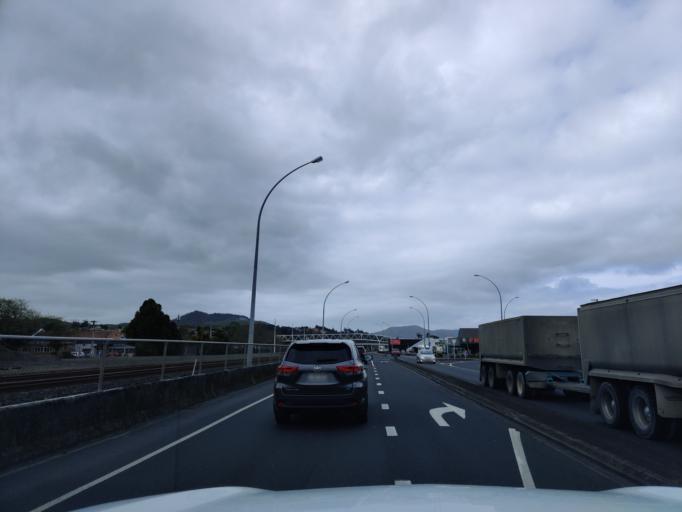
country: NZ
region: Waikato
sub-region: Waikato District
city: Ngaruawahia
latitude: -37.5561
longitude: 175.1593
